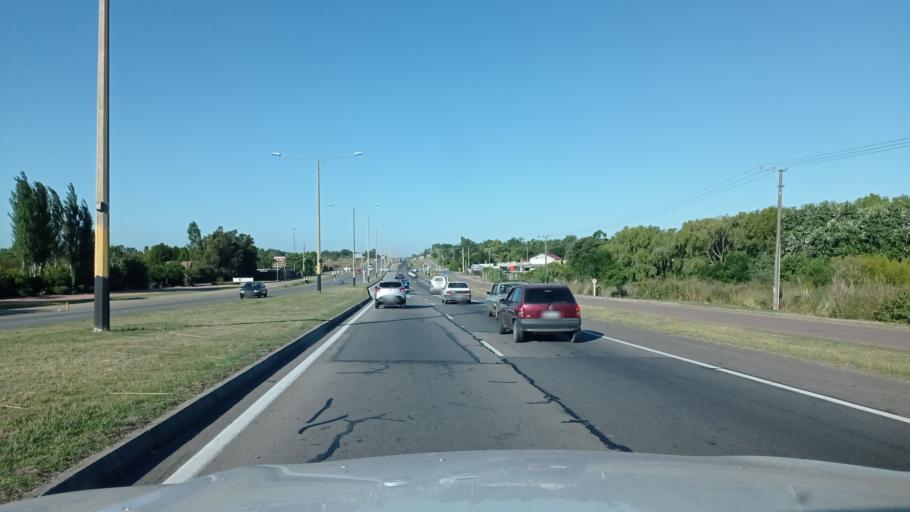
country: UY
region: Canelones
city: Colonia Nicolich
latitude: -34.8129
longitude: -55.9684
